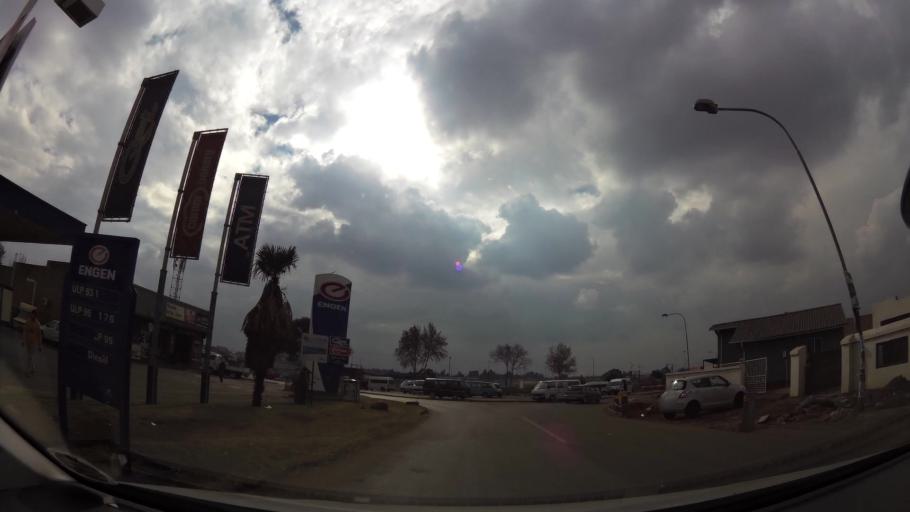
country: ZA
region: Gauteng
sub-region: City of Johannesburg Metropolitan Municipality
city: Soweto
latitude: -26.2634
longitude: 27.8479
